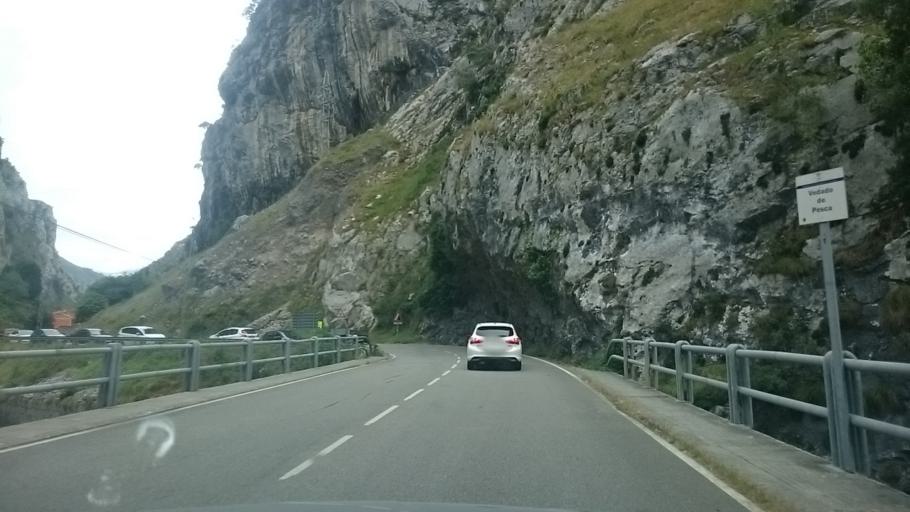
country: ES
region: Asturias
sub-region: Province of Asturias
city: Carrena
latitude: 43.2595
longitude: -4.8308
